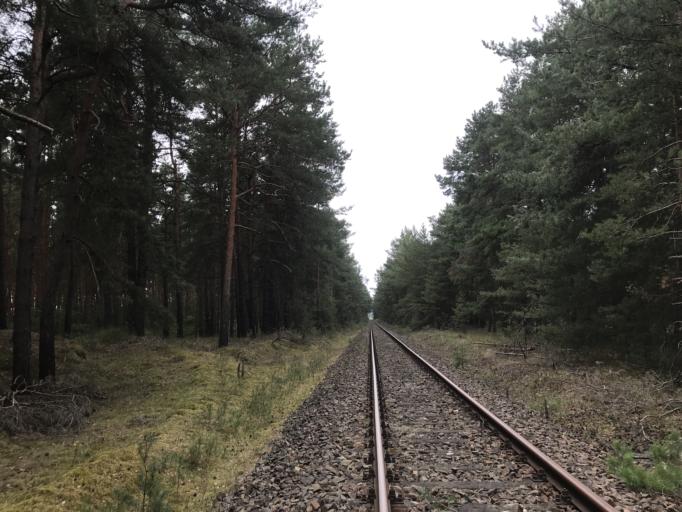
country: DE
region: Brandenburg
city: Sperenberg
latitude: 52.0850
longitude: 13.3358
